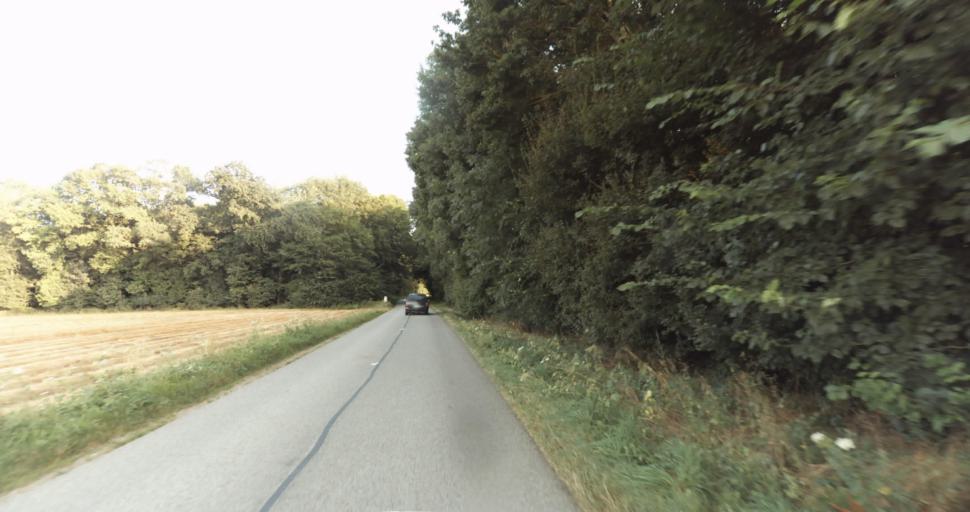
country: FR
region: Haute-Normandie
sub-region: Departement de l'Eure
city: Saint-Germain-sur-Avre
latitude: 48.8404
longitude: 1.2557
